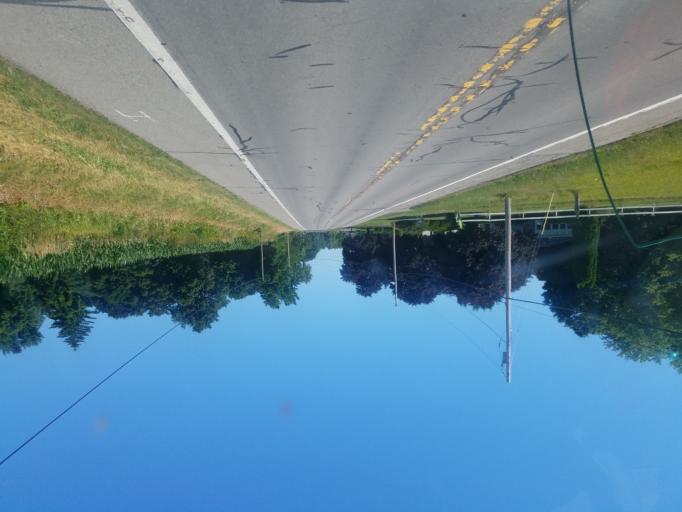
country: US
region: New York
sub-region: Ontario County
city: Phelps
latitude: 42.9917
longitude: -77.0894
